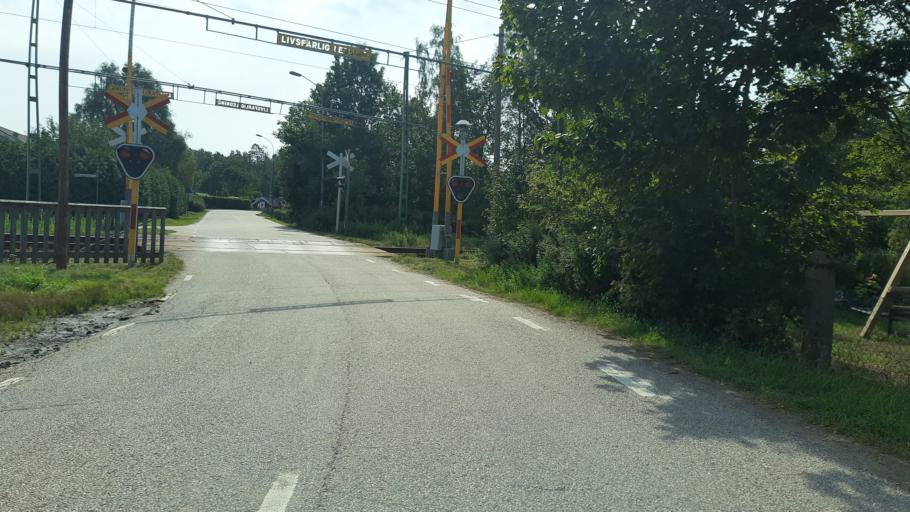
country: SE
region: Blekinge
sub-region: Karlskrona Kommun
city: Nattraby
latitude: 56.2264
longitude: 15.4185
